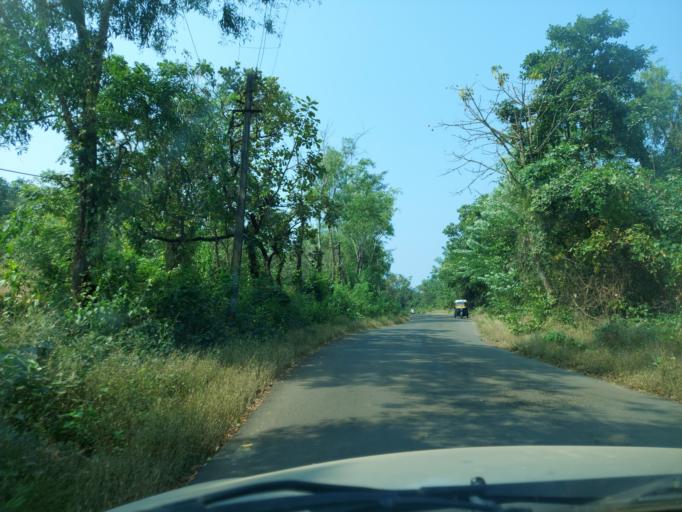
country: IN
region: Maharashtra
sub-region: Sindhudurg
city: Kudal
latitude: 15.9661
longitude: 73.5828
